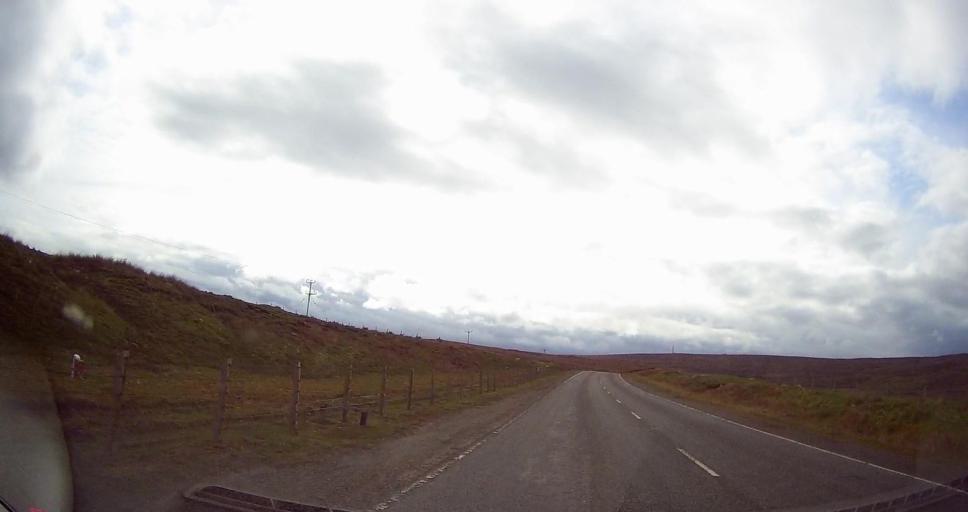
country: GB
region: Scotland
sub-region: Shetland Islands
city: Lerwick
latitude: 60.4446
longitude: -1.2422
